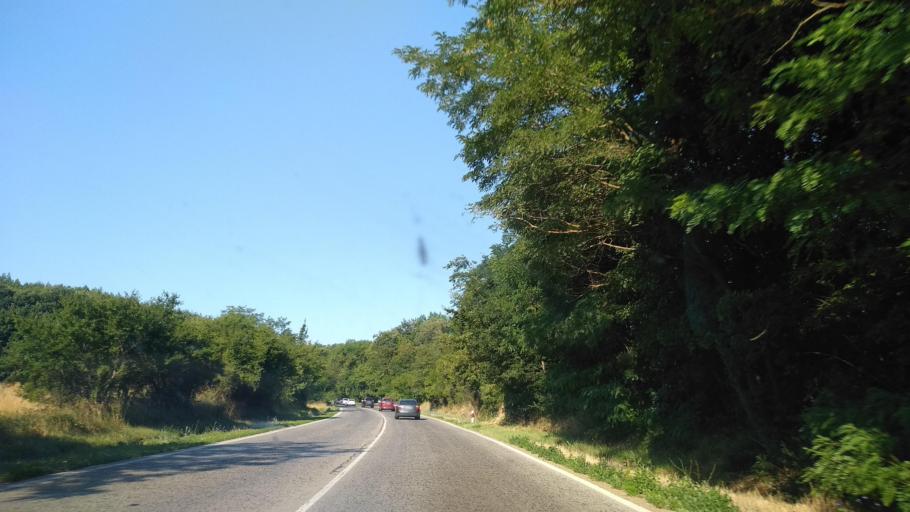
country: BG
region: Lovech
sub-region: Obshtina Lovech
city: Lovech
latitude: 43.0484
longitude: 24.8581
